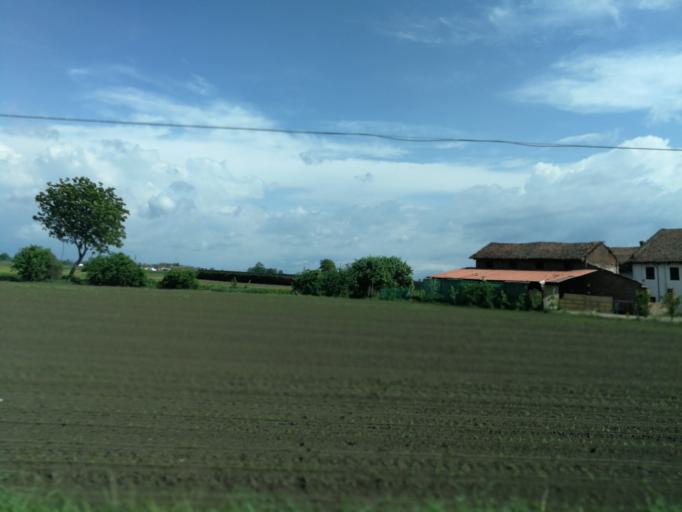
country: IT
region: Piedmont
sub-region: Provincia di Cuneo
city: Moretta
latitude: 44.7837
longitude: 7.5604
